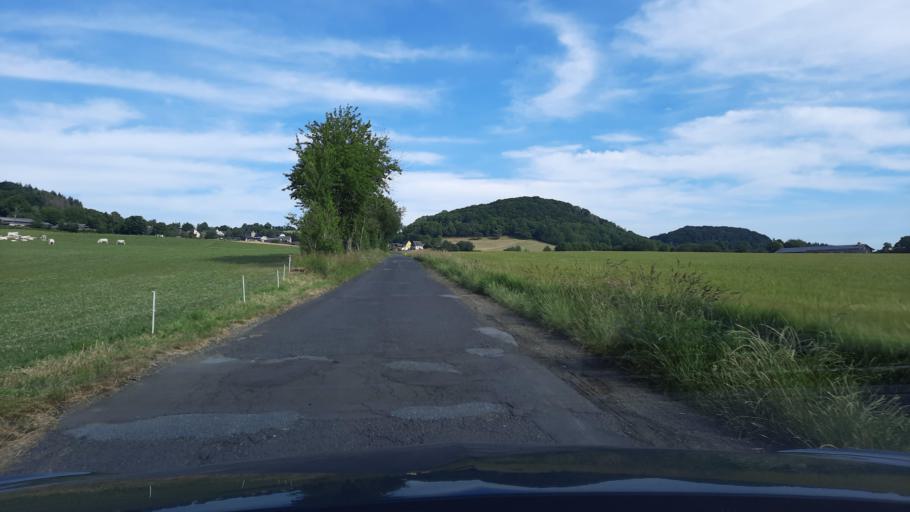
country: DE
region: Rheinland-Pfalz
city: Volkesfeld
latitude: 50.4210
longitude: 7.1566
